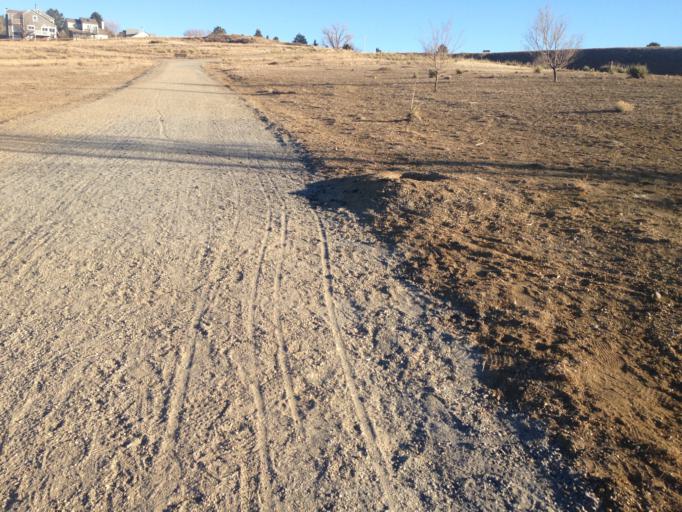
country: US
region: Colorado
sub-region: Broomfield County
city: Broomfield
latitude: 39.9358
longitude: -105.0997
